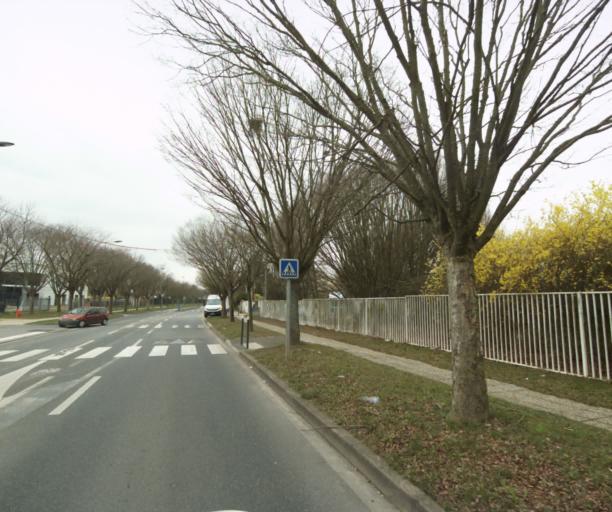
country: FR
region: Ile-de-France
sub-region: Departement du Val-d'Oise
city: Osny
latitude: 49.0541
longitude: 2.0447
